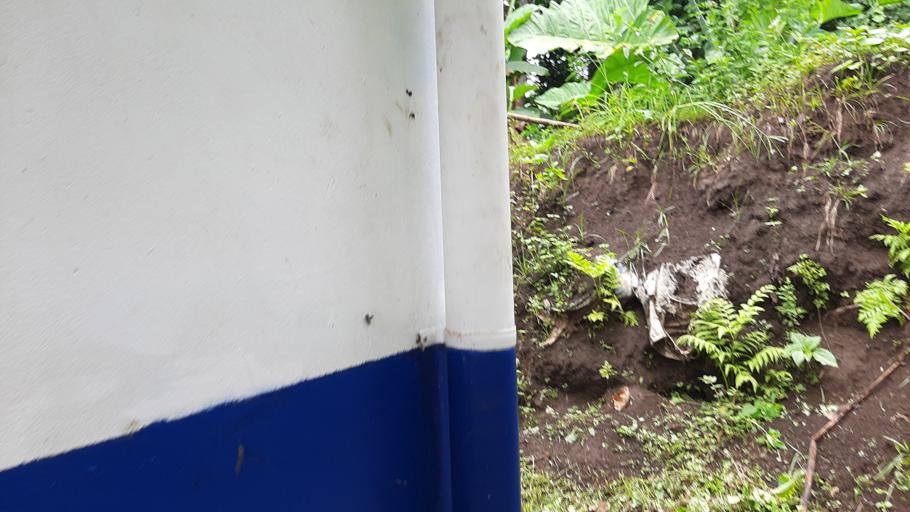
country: VU
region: Malampa
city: Lakatoro
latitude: -16.5918
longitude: 168.1714
